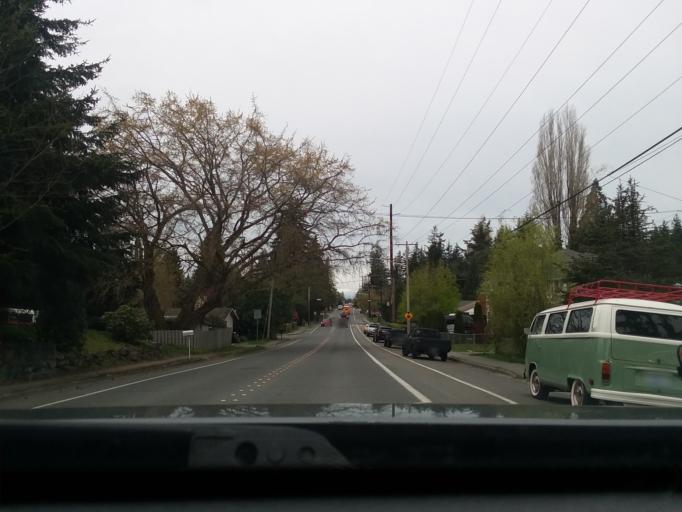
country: US
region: Washington
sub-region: Snohomish County
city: Lynnwood
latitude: 47.8103
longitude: -122.3122
